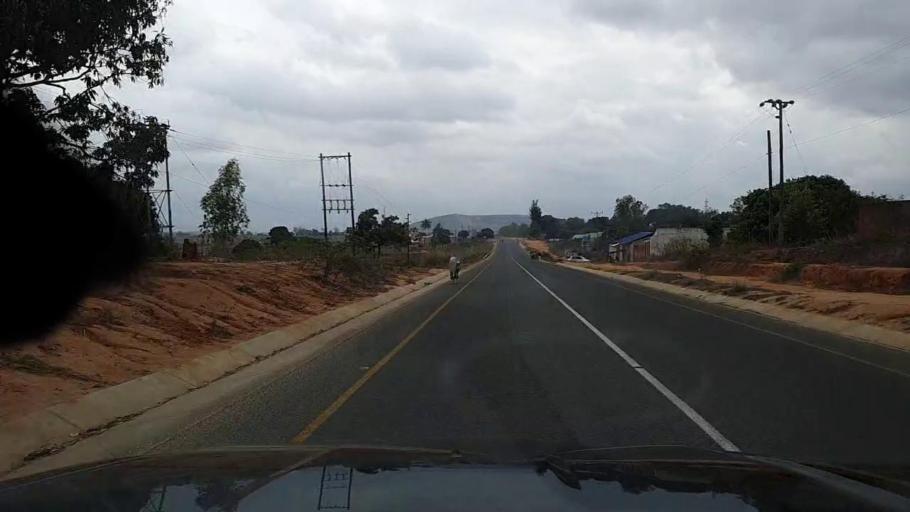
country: MZ
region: Nampula
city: Nampula
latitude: -15.1719
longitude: 39.3081
